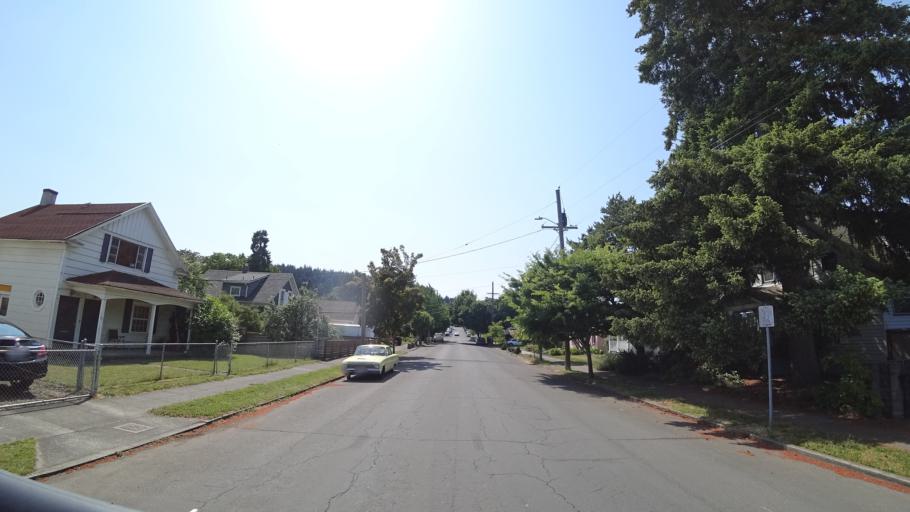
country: US
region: Oregon
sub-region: Multnomah County
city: Lents
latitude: 45.5160
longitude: -122.5817
